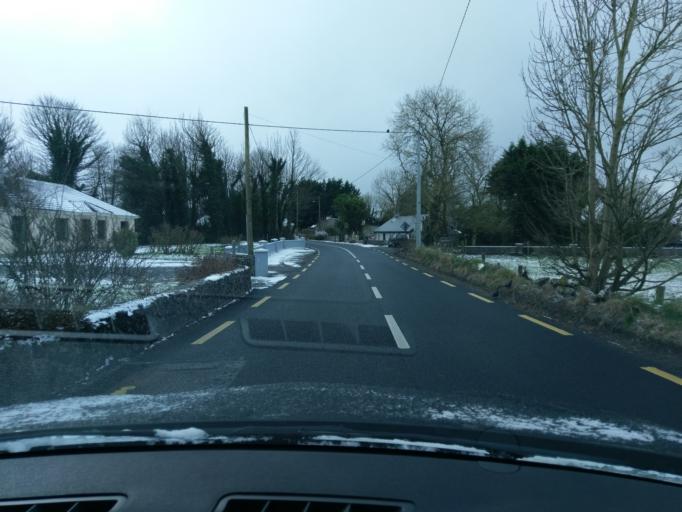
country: IE
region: Connaught
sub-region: County Galway
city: Athenry
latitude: 53.2962
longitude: -8.7562
